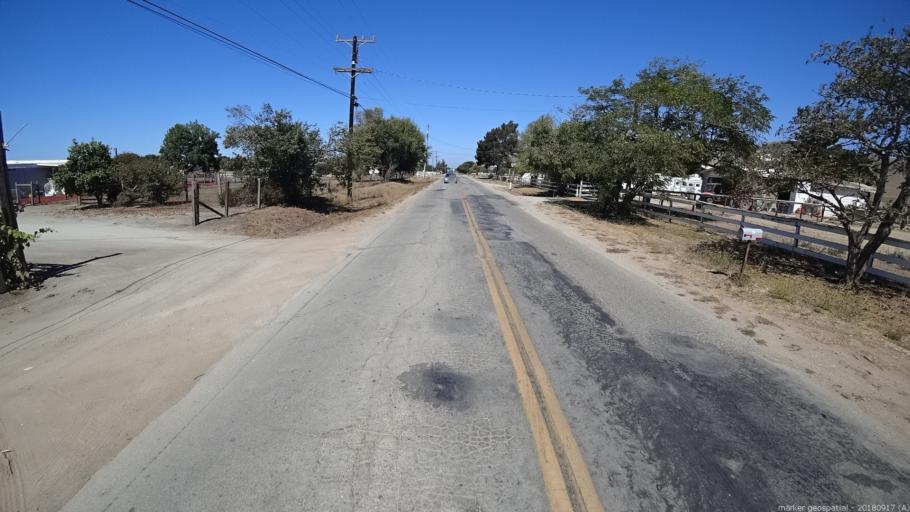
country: US
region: California
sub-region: Monterey County
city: Salinas
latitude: 36.7343
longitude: -121.5982
